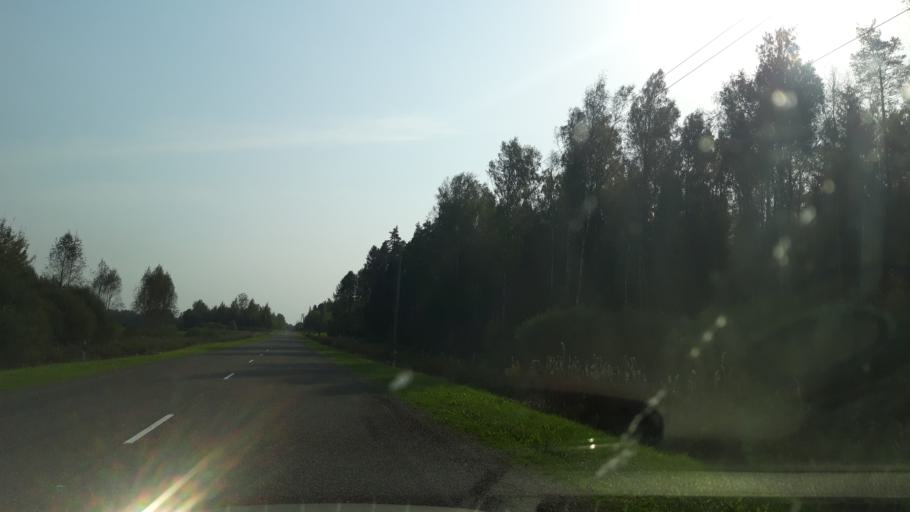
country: LV
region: Burtnieki
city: Matisi
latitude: 57.6416
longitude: 25.2484
